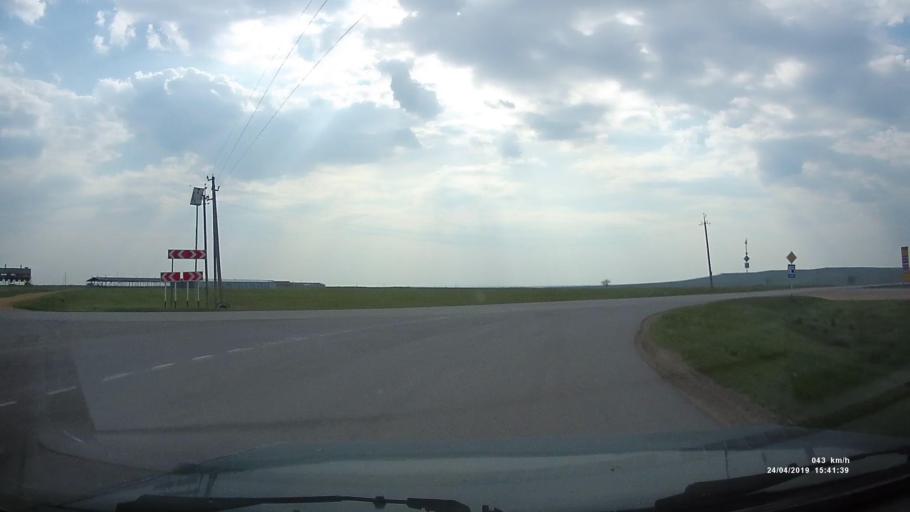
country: RU
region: Kalmykiya
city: Yashalta
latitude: 46.5709
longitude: 42.7955
